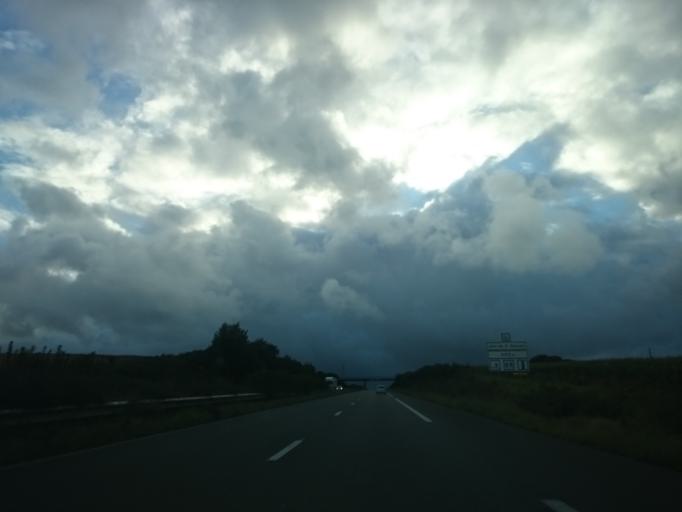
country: FR
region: Brittany
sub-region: Departement du Finistere
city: Bodilis
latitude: 48.5055
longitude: -4.1334
